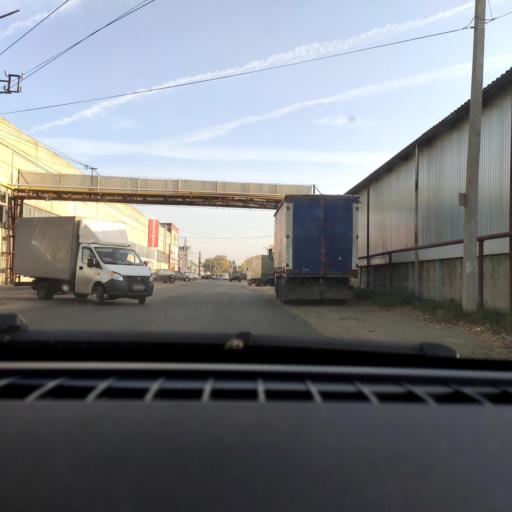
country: RU
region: Voronezj
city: Voronezh
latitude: 51.6548
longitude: 39.2840
